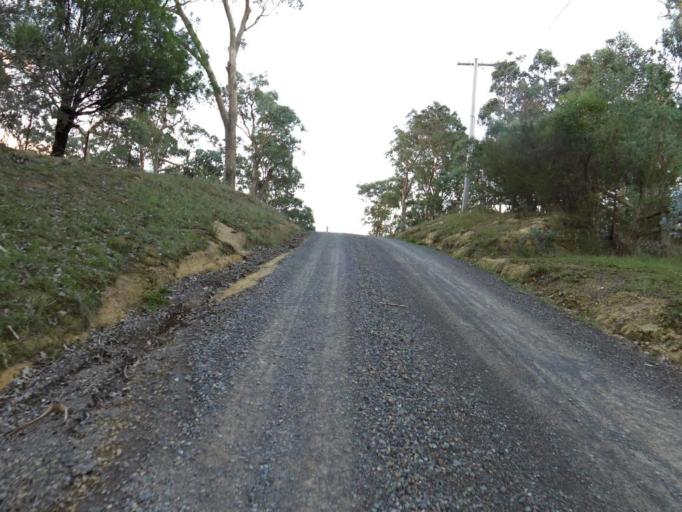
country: AU
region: Victoria
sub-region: Manningham
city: Warrandyte
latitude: -37.7385
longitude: 145.2383
